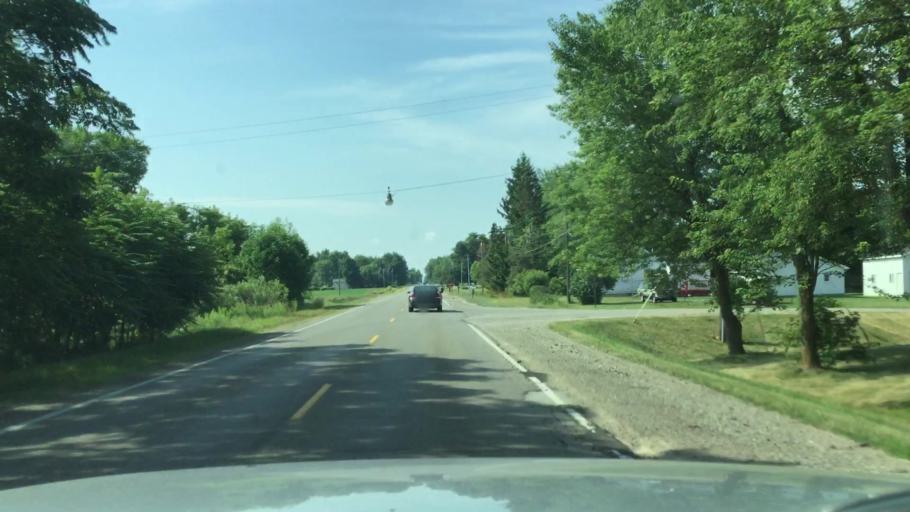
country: US
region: Michigan
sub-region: Genesee County
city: Flushing
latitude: 43.1118
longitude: -83.8137
